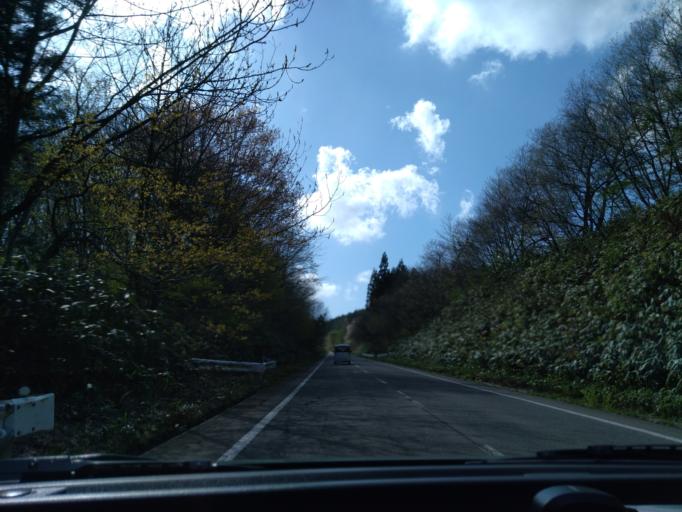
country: JP
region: Akita
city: Akita
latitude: 39.6960
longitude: 140.2605
